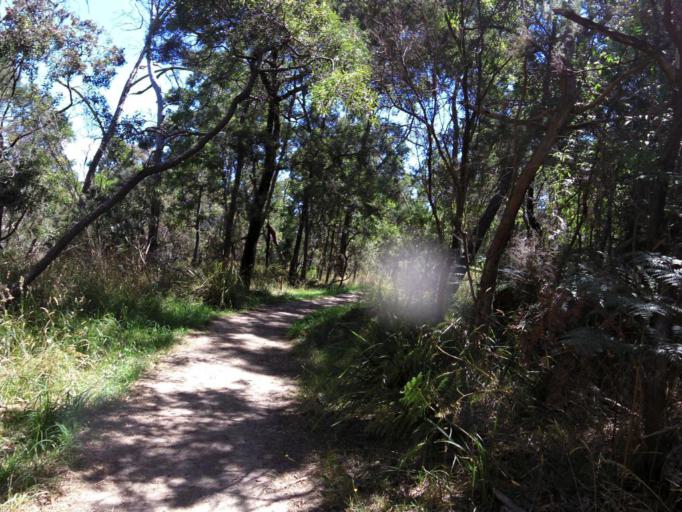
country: AU
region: Victoria
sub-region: Mornington Peninsula
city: Moorooduc
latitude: -38.2065
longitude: 145.1104
